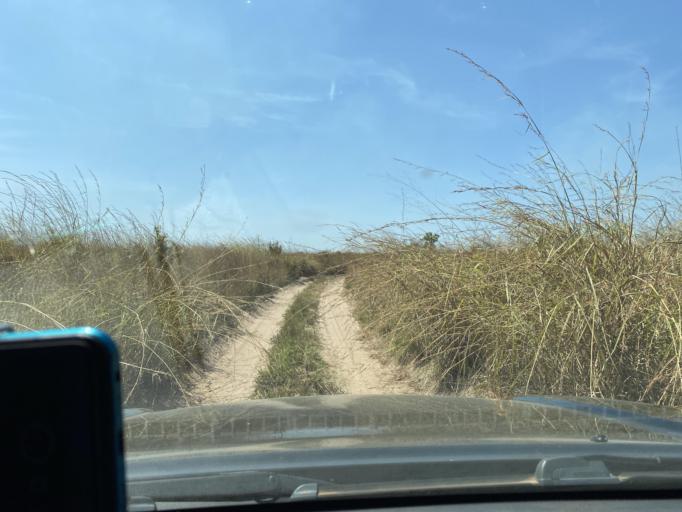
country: CD
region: Kasai-Oriental
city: Kabinda
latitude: -5.9219
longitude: 24.8406
